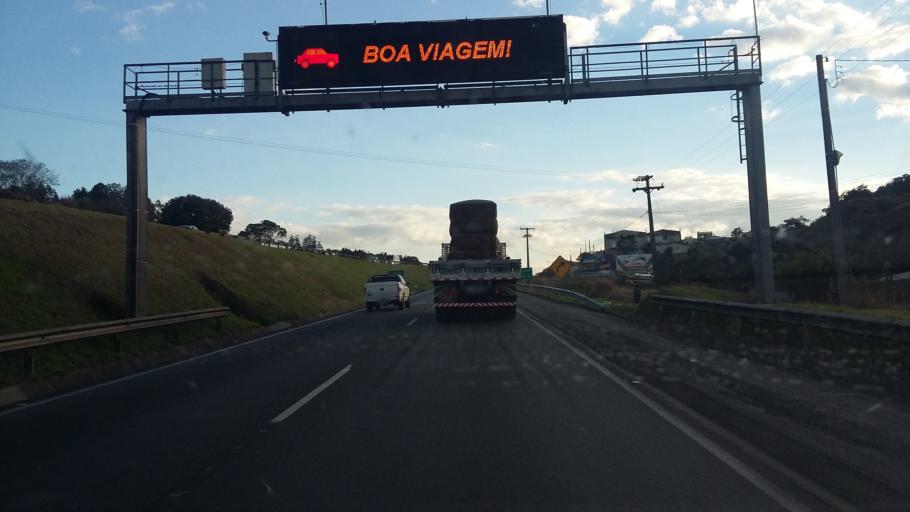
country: BR
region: Parana
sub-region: Curitiba
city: Curitiba
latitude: -25.4314
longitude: -49.3994
